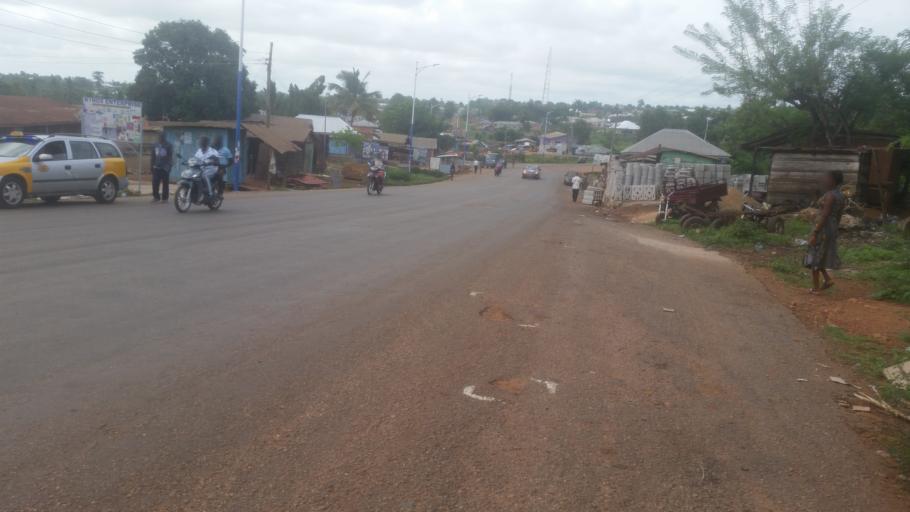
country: GH
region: Western
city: Bibiani
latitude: 6.7995
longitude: -2.5179
